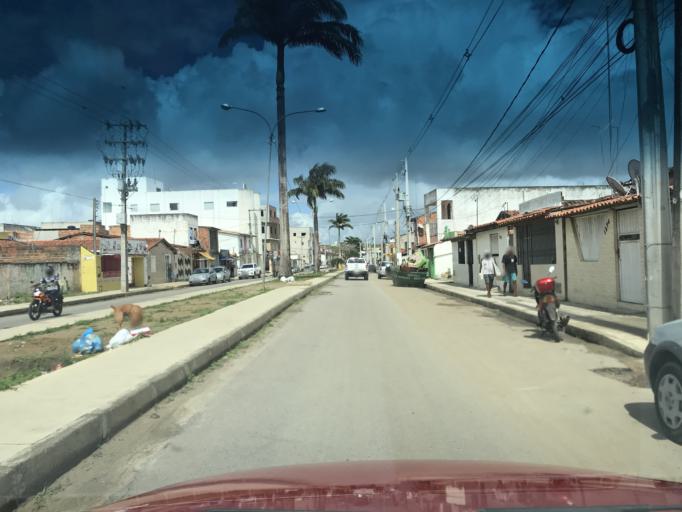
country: BR
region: Bahia
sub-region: Santo Antonio De Jesus
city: Santo Antonio de Jesus
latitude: -12.9768
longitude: -39.2750
